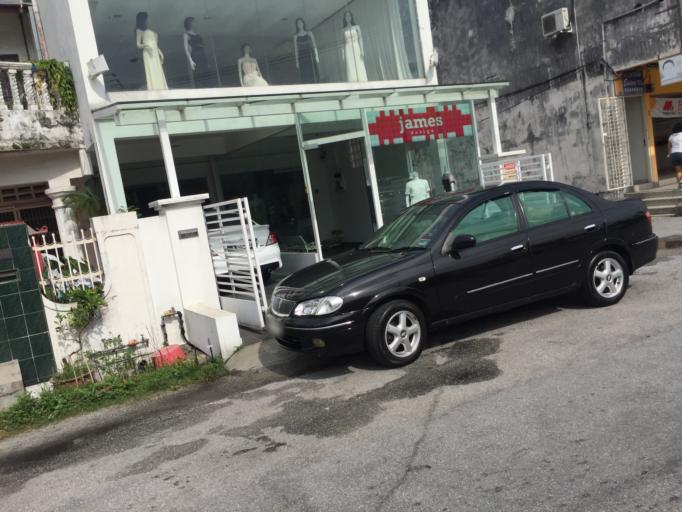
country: MY
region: Perak
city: Ipoh
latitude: 4.6115
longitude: 101.1088
